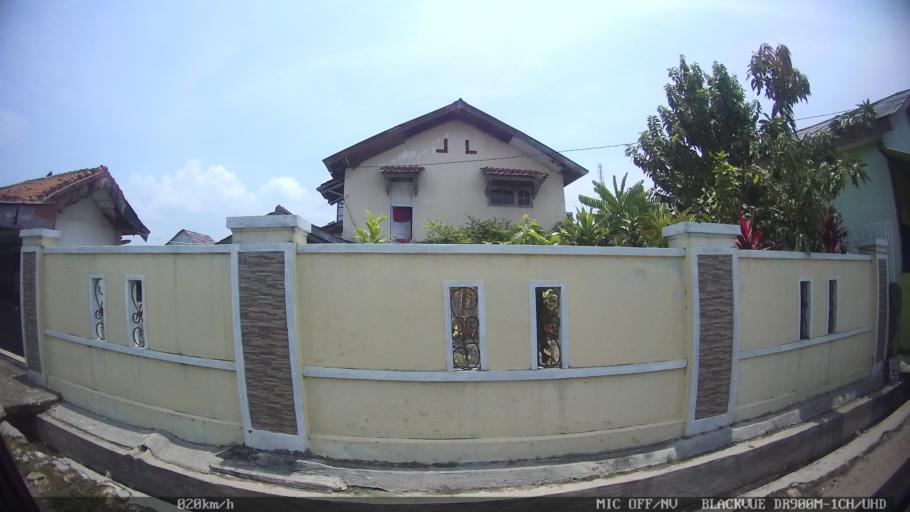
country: ID
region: Lampung
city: Bandarlampung
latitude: -5.4559
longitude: 105.2624
